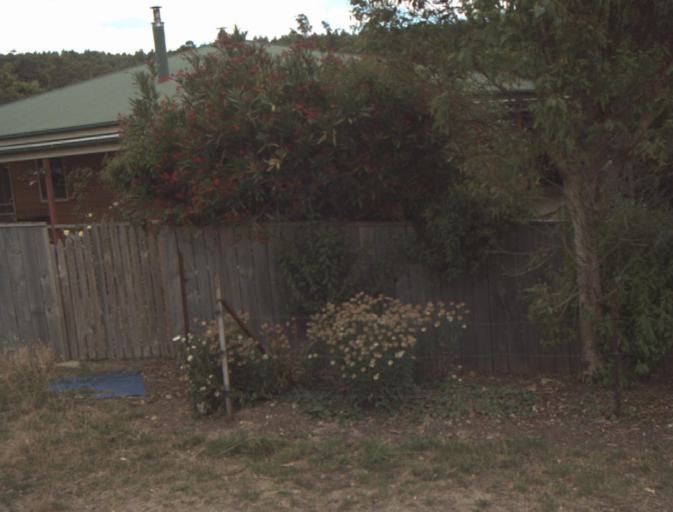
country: AU
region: Tasmania
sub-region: Launceston
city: Mayfield
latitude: -41.2412
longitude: 147.1858
